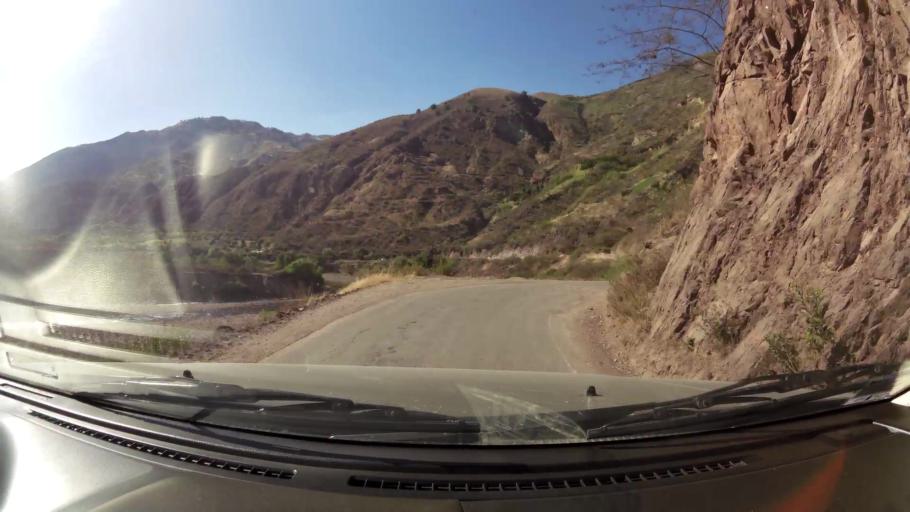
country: PE
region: Huancavelica
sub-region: Provincia de Acobamba
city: Pomacocha
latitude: -12.7742
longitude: -74.4992
